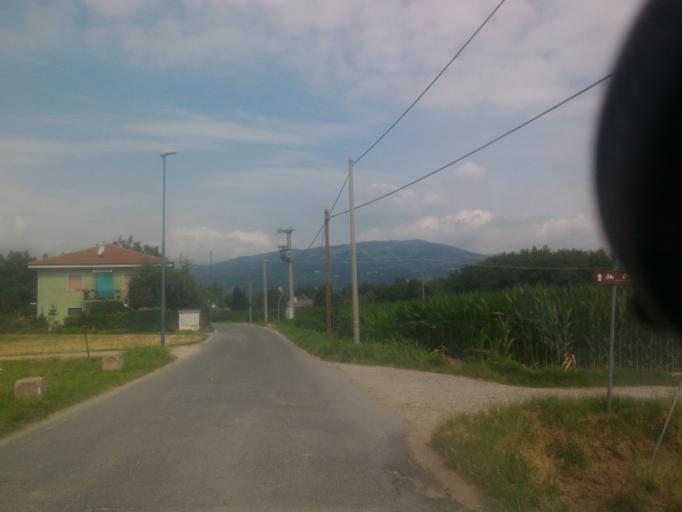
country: IT
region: Piedmont
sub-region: Provincia di Torino
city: Pinerolo
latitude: 44.8704
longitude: 7.3182
